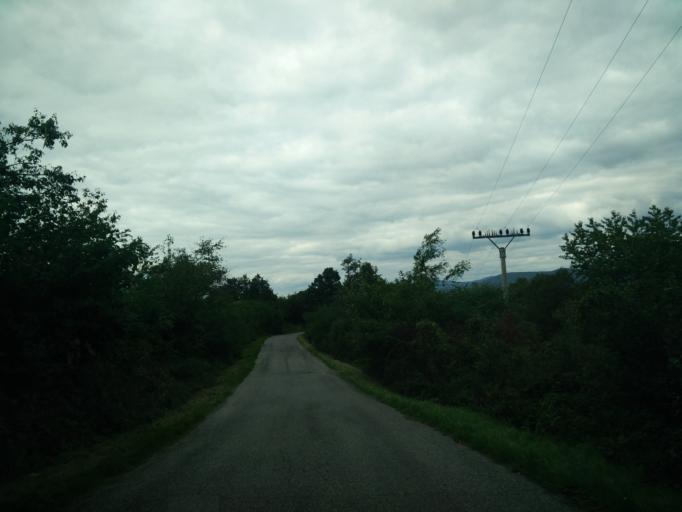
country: SK
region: Nitriansky
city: Novaky
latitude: 48.6209
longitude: 18.4995
